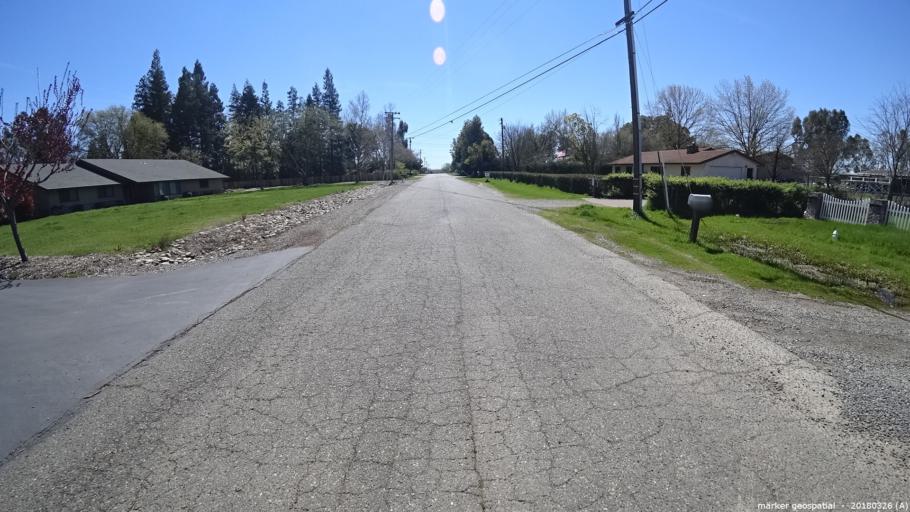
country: US
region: California
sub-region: Sacramento County
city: Wilton
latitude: 38.4560
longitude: -121.2828
